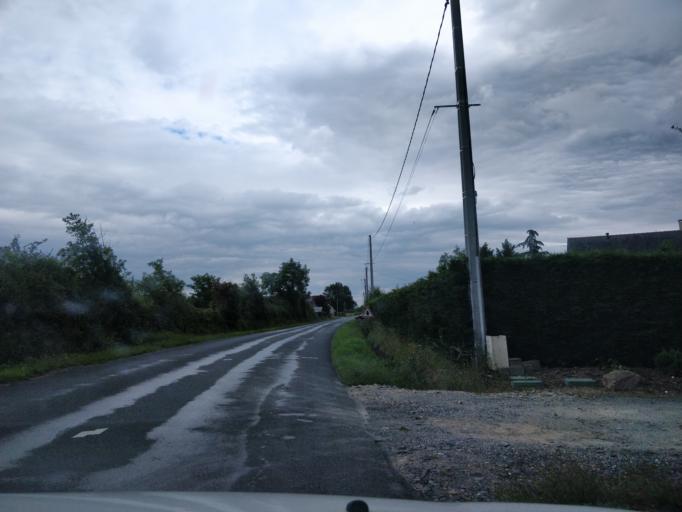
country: FR
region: Pays de la Loire
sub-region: Departement de Maine-et-Loire
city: Grez-Neuville
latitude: 47.6326
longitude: -0.6283
